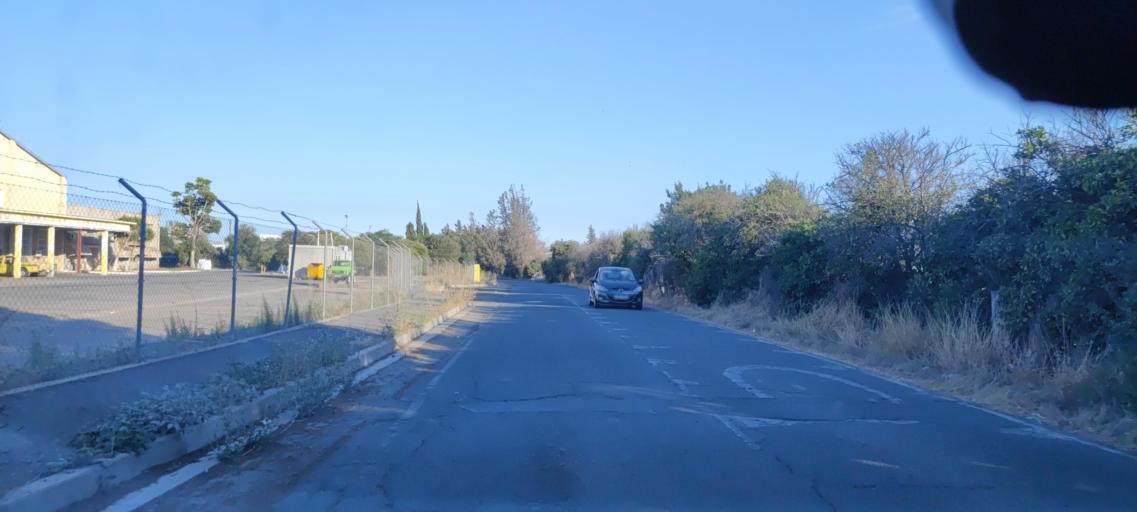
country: CY
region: Limassol
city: Pano Polemidia
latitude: 34.6642
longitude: 32.9985
